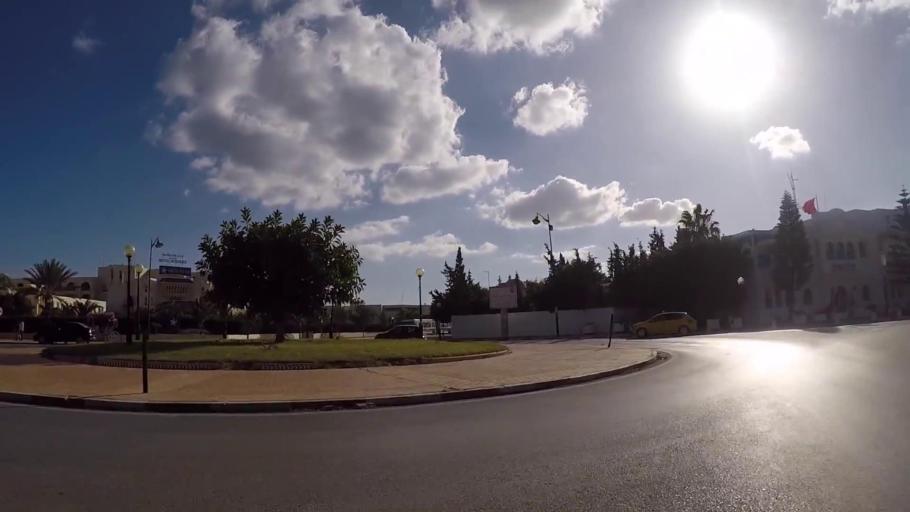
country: TN
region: Nabul
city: Al Hammamat
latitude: 36.3646
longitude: 10.5329
